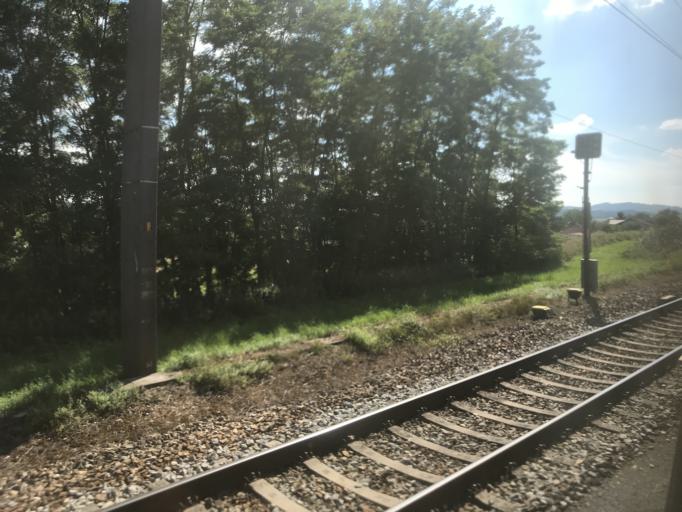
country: AT
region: Upper Austria
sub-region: Politischer Bezirk Urfahr-Umgebung
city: Engerwitzdorf
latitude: 48.3299
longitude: 14.5096
